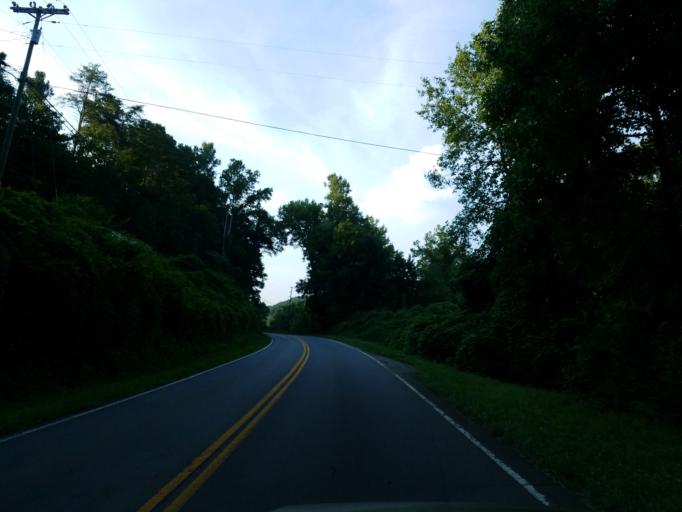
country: US
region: Georgia
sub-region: Gilmer County
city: Ellijay
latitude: 34.6017
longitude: -84.5274
